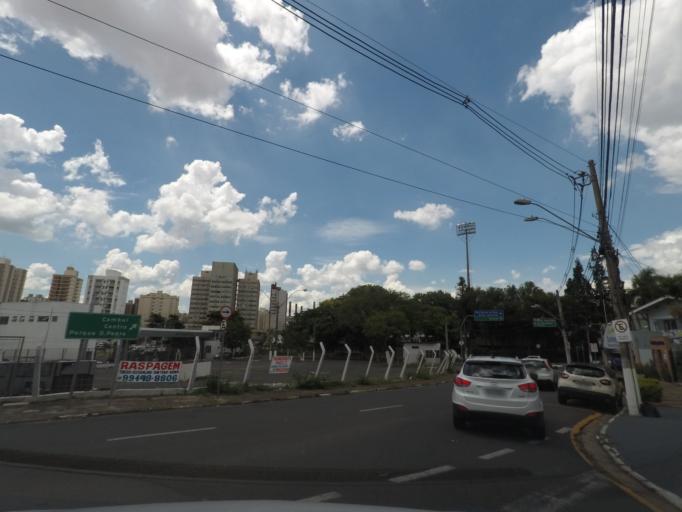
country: BR
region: Sao Paulo
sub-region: Campinas
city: Campinas
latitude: -22.9114
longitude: -47.0442
